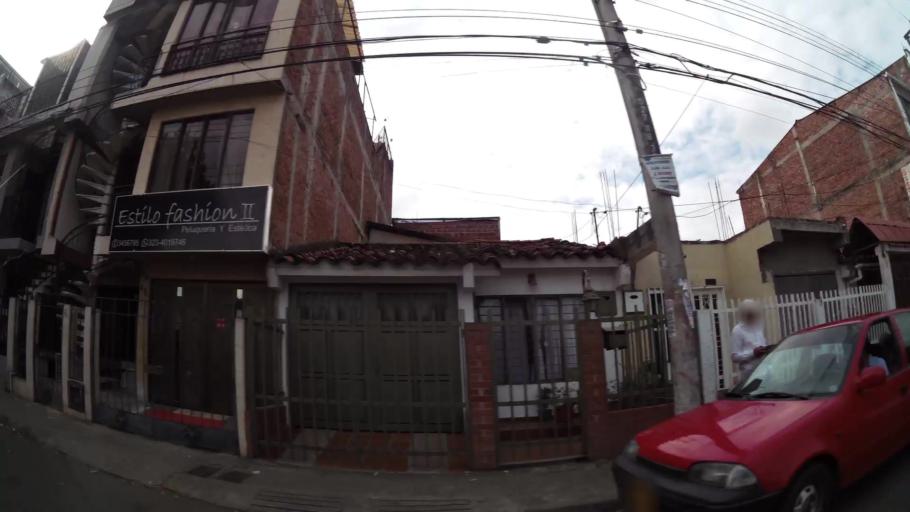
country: CO
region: Valle del Cauca
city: Cali
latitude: 3.4739
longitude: -76.4904
